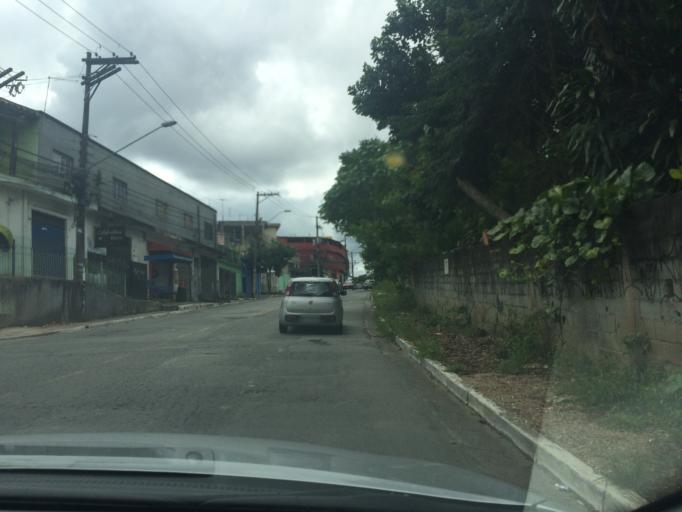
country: BR
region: Sao Paulo
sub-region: Guarulhos
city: Guarulhos
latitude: -23.4318
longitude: -46.5284
